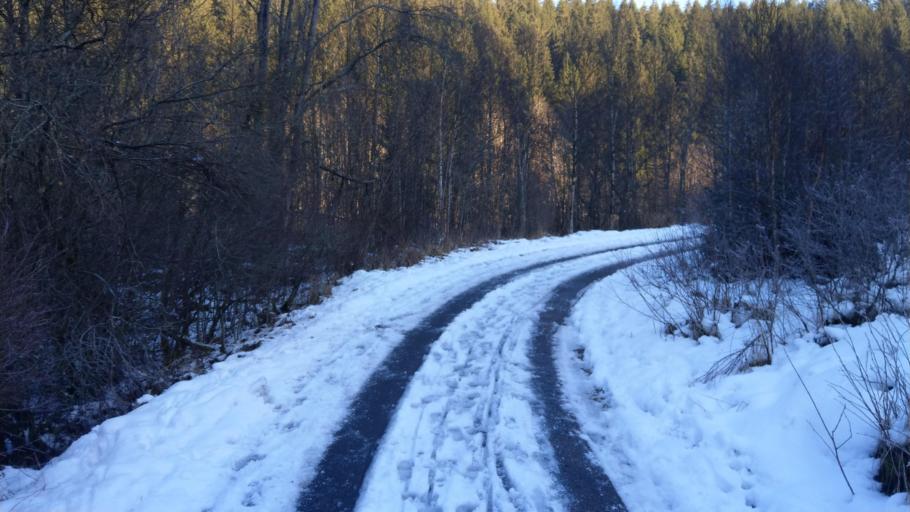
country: DE
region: North Rhine-Westphalia
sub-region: Regierungsbezirk Koln
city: Monschau
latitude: 50.5082
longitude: 6.2492
